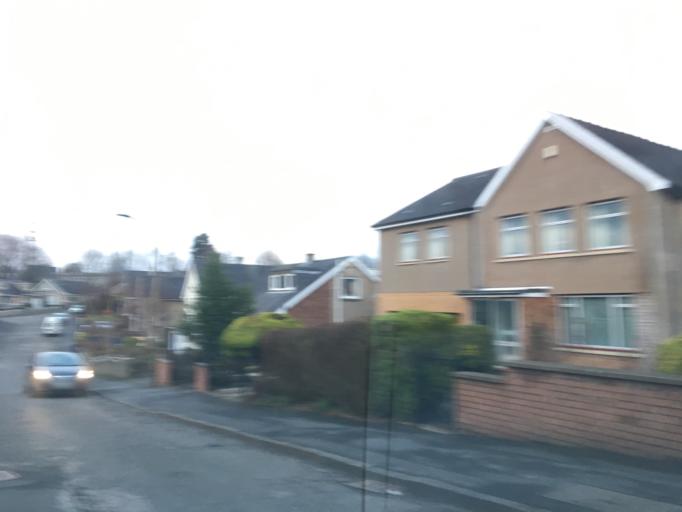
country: GB
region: Scotland
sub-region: Stirling
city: Stirling
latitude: 56.1078
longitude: -3.9436
